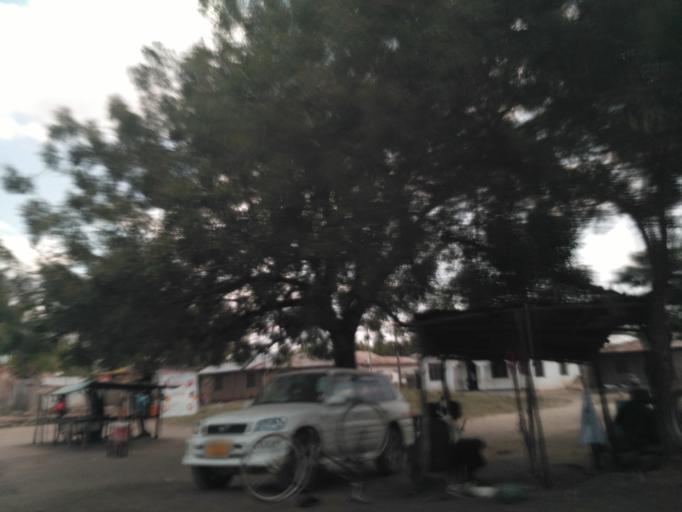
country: TZ
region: Dar es Salaam
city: Dar es Salaam
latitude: -6.8259
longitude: 39.3138
